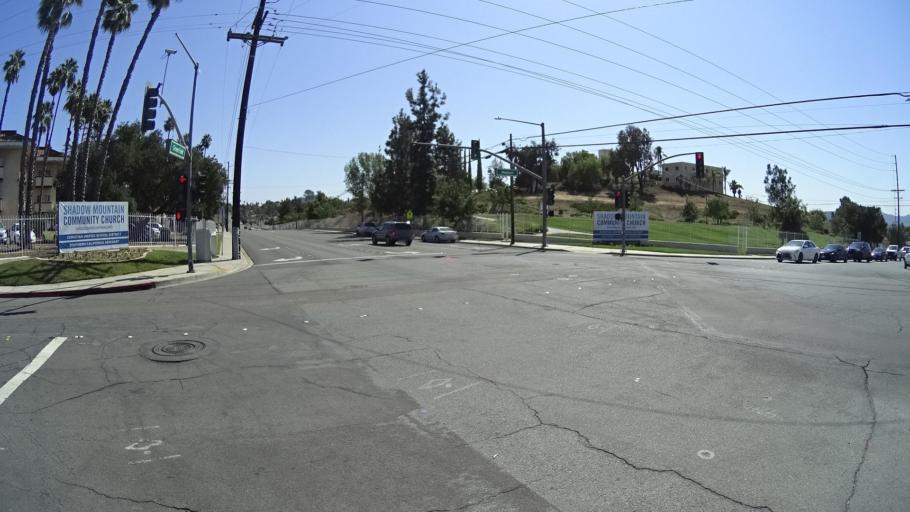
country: US
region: California
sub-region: San Diego County
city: Granite Hills
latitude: 32.8011
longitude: -116.9048
